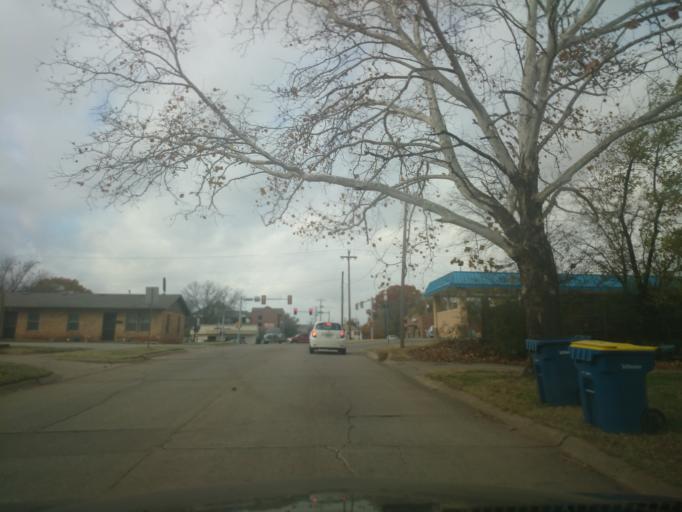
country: US
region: Oklahoma
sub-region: Payne County
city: Stillwater
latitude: 36.1238
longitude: -97.0576
